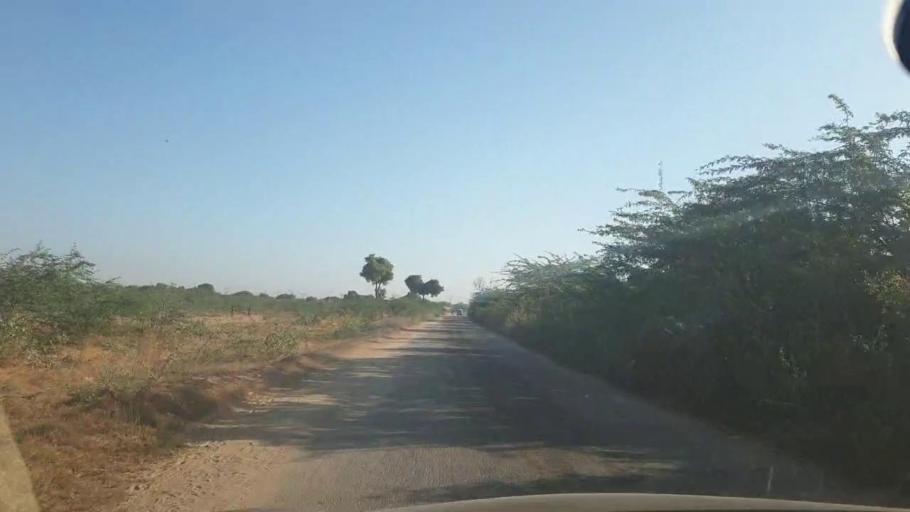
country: PK
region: Sindh
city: Malir Cantonment
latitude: 25.1088
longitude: 67.2639
